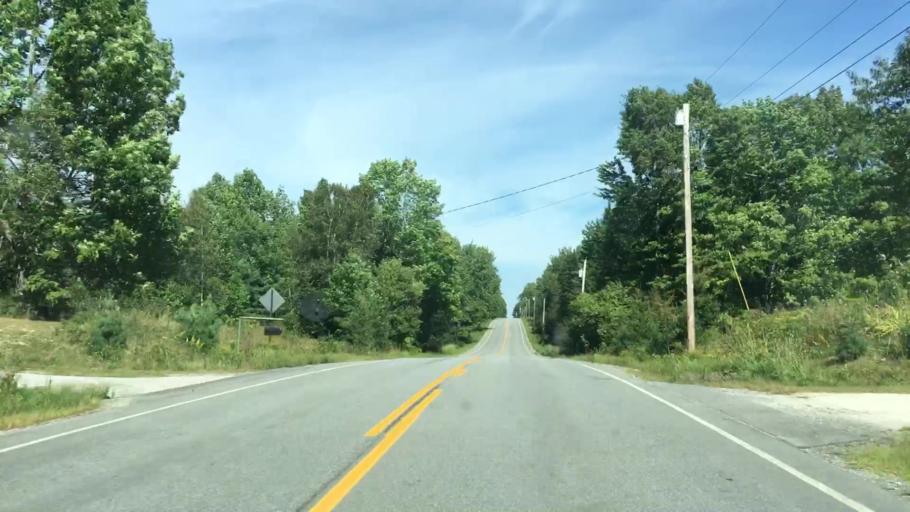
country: US
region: Maine
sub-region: Penobscot County
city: Howland
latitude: 45.2119
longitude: -68.7989
